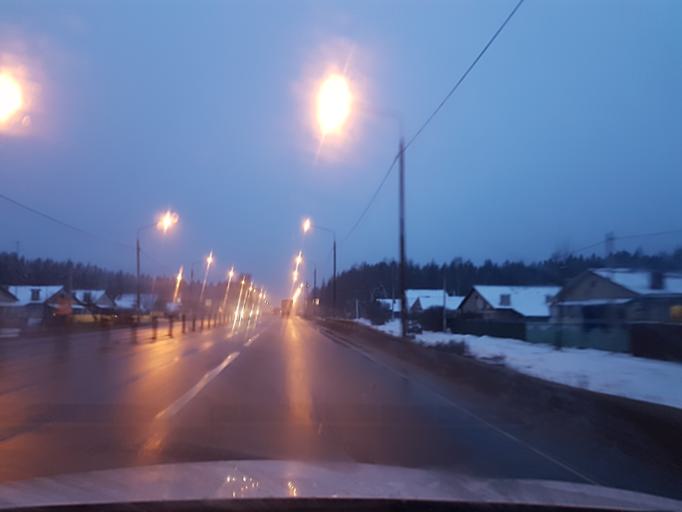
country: RU
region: Moskovskaya
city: Klin
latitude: 56.3968
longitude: 36.6570
